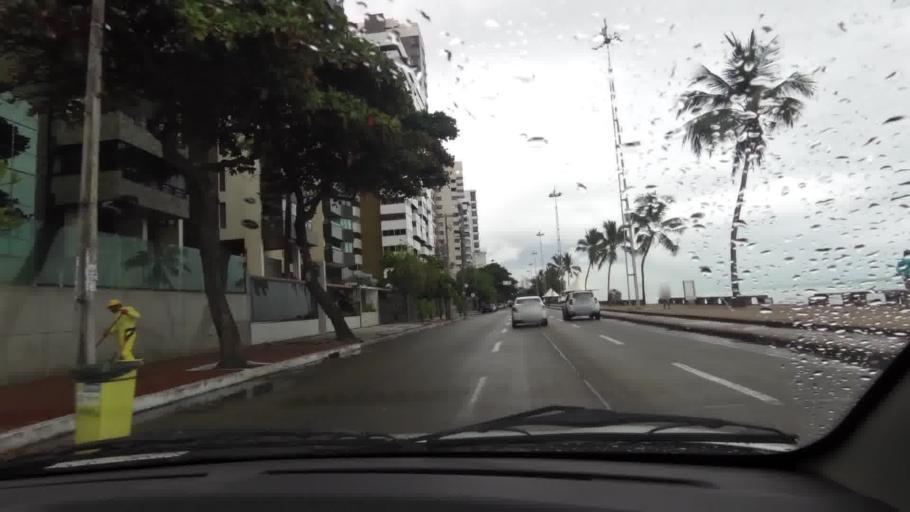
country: BR
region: Pernambuco
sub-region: Recife
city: Recife
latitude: -8.1326
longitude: -34.9025
